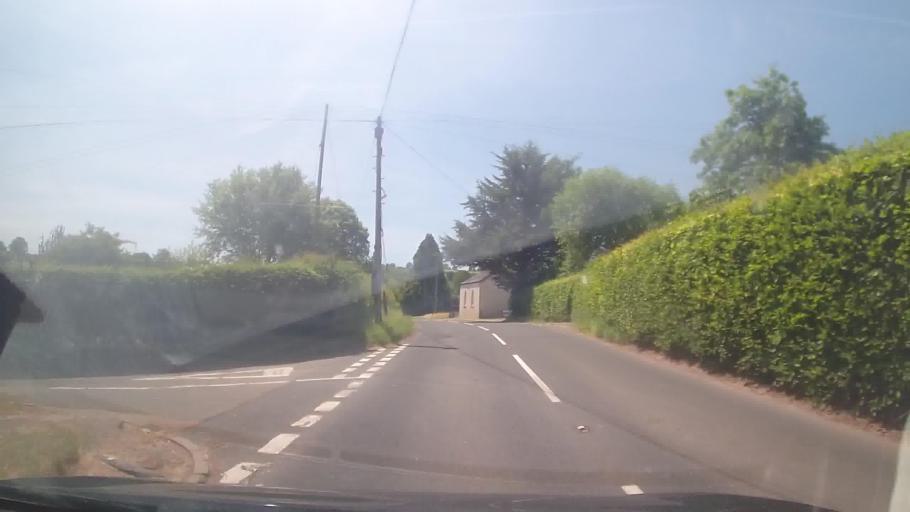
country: GB
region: England
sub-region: Herefordshire
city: Llanrothal
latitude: 51.8861
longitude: -2.7324
